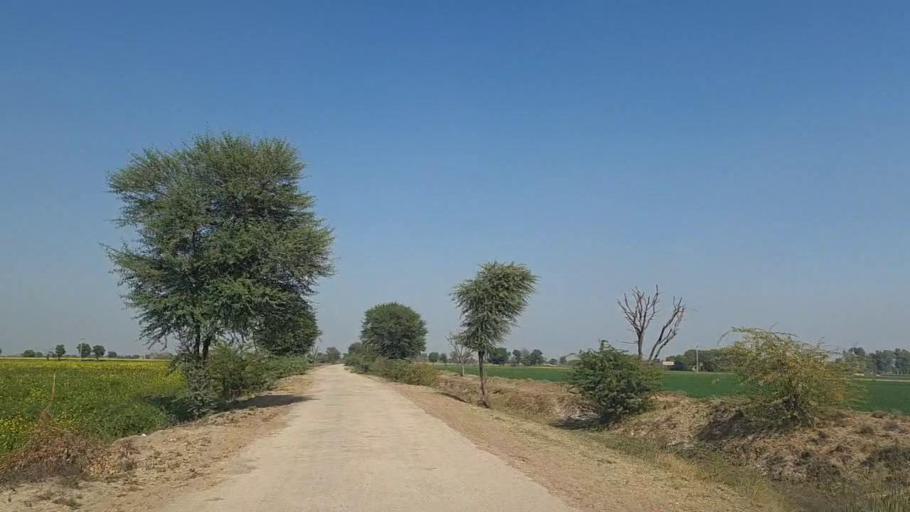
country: PK
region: Sindh
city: Shahpur Chakar
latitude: 26.1875
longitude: 68.6038
